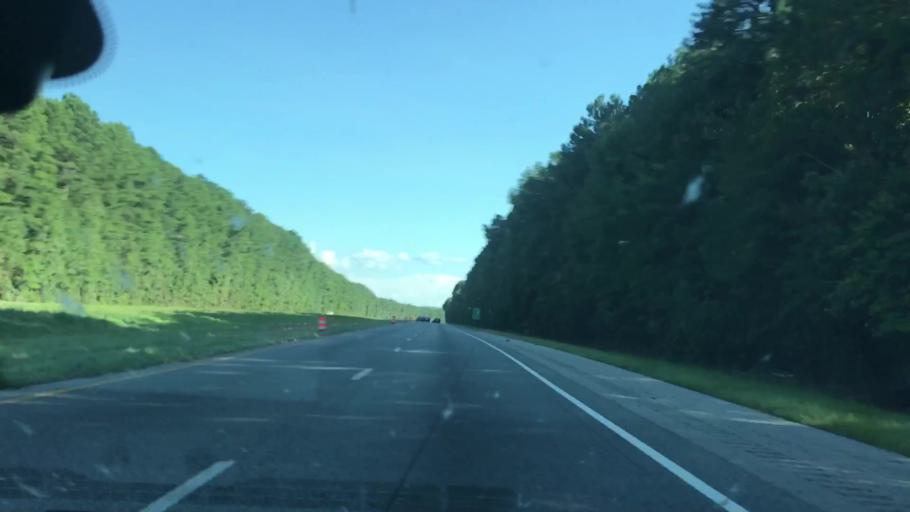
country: US
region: Georgia
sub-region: Harris County
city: Hamilton
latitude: 32.7679
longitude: -85.0200
